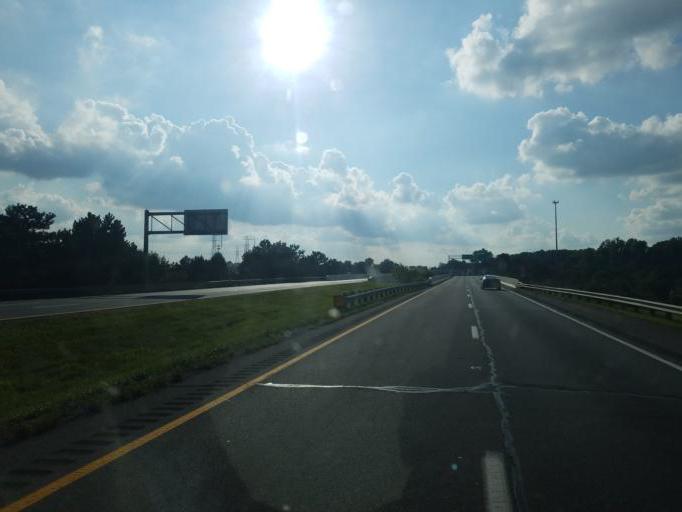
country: US
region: Ohio
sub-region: Richland County
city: Lincoln Heights
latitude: 40.7791
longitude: -82.4692
